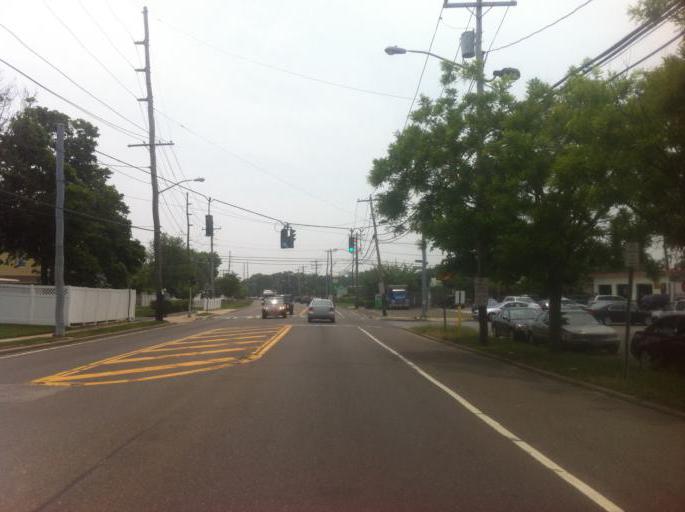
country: US
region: New York
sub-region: Nassau County
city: Plainedge
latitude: 40.7089
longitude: -73.4829
